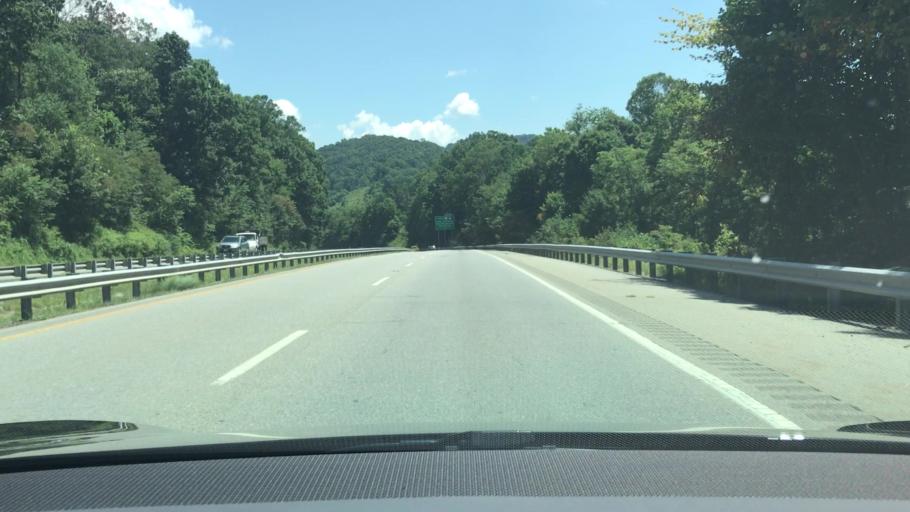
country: US
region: North Carolina
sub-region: Haywood County
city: Lake Junaluska
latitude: 35.5130
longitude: -82.9759
